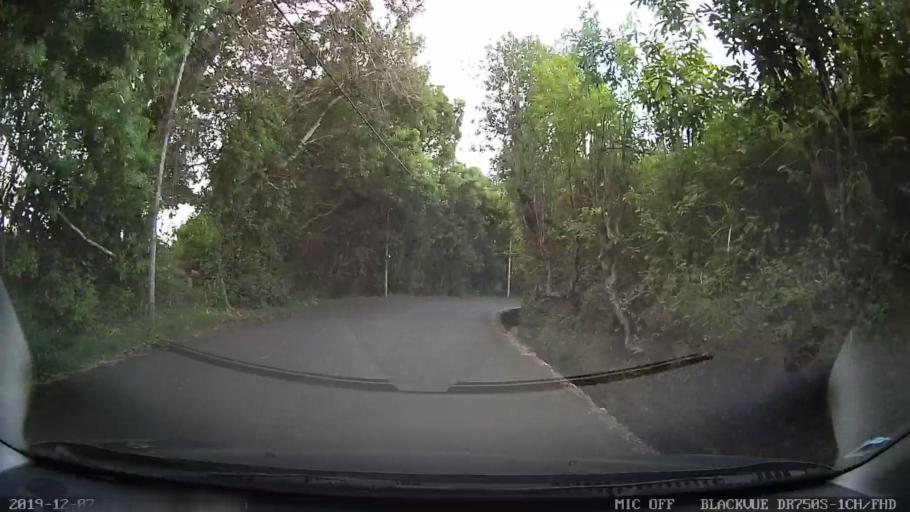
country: RE
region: Reunion
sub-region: Reunion
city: Sainte-Marie
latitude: -20.9373
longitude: 55.5340
